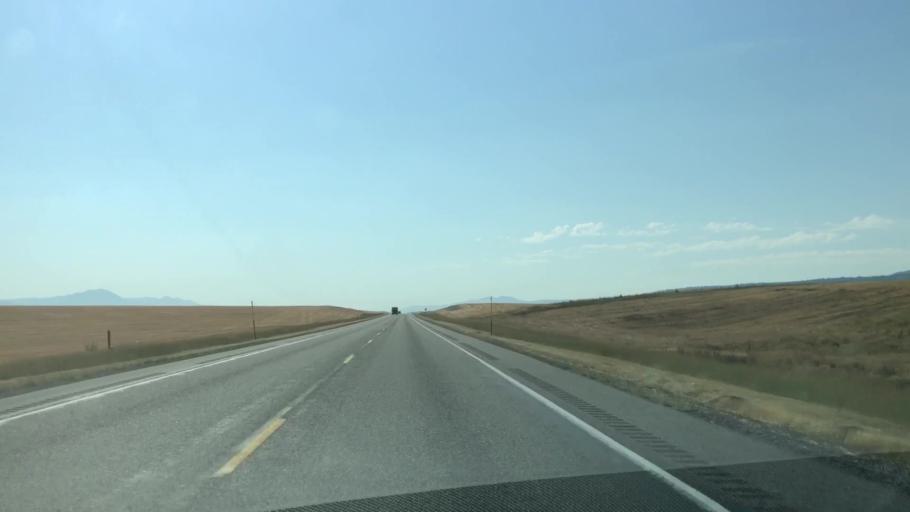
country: US
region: Idaho
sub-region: Madison County
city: Rexburg
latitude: 43.5590
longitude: -111.5413
